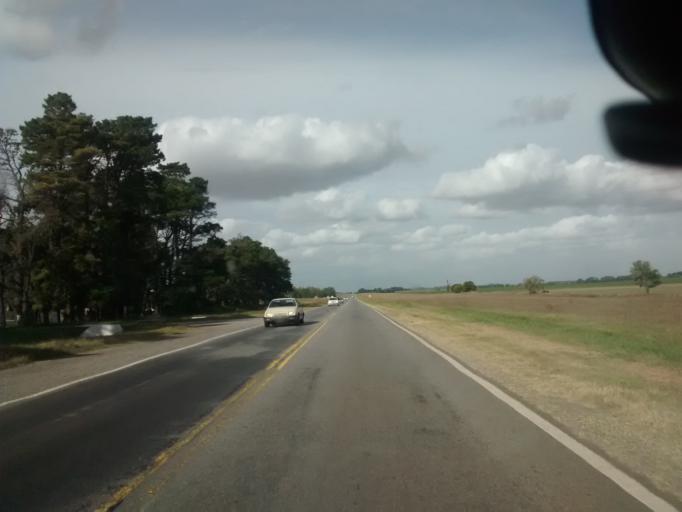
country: AR
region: Buenos Aires
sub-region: Partido de Balcarce
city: Balcarce
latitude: -37.6691
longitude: -58.5375
